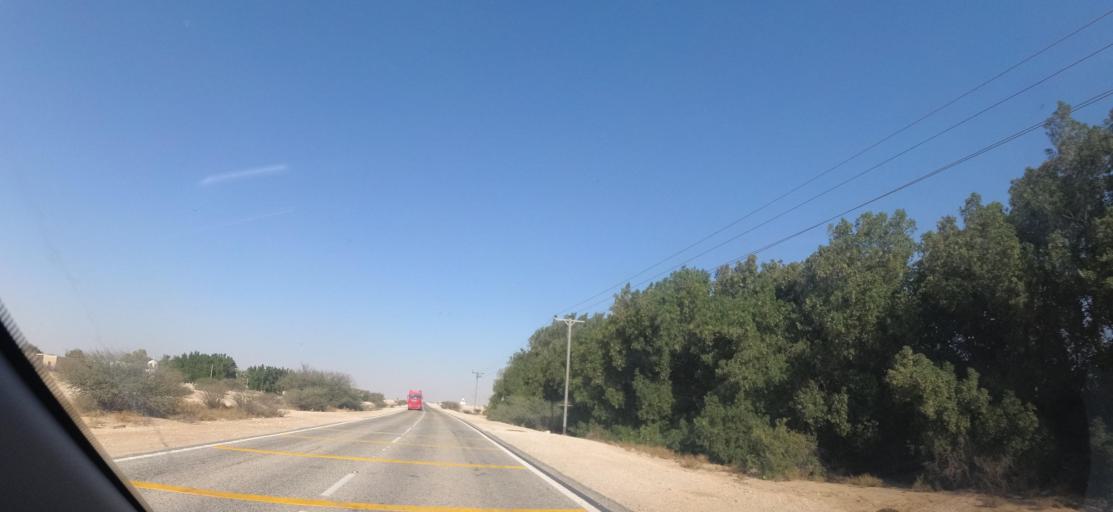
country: QA
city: Al Jumayliyah
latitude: 25.6258
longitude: 51.0915
